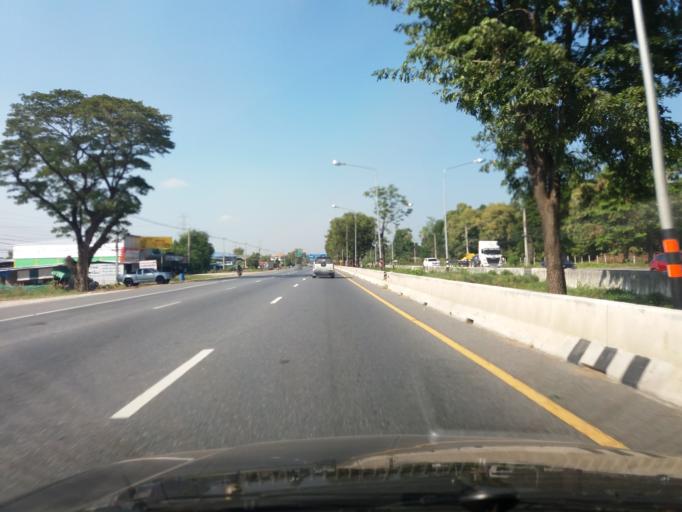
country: TH
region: Nakhon Sawan
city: Krok Phra
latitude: 15.5966
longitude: 100.1228
